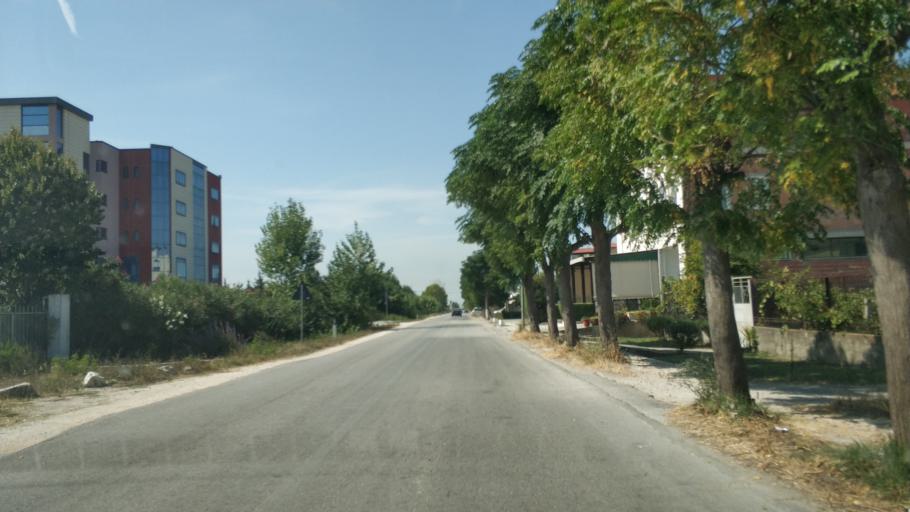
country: AL
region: Fier
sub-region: Rrethi i Fierit
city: Dermenas
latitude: 40.7358
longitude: 19.5237
